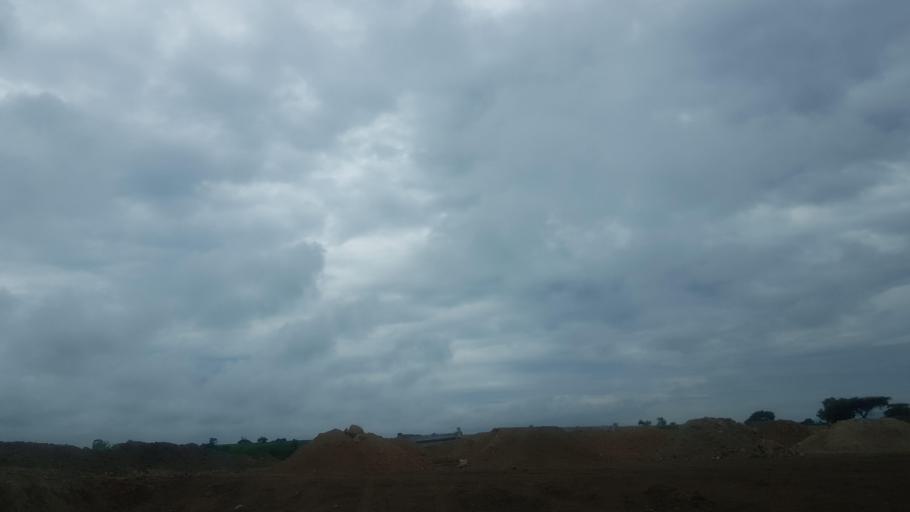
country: ET
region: Oromiya
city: Shashemene
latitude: 7.3678
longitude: 38.6448
